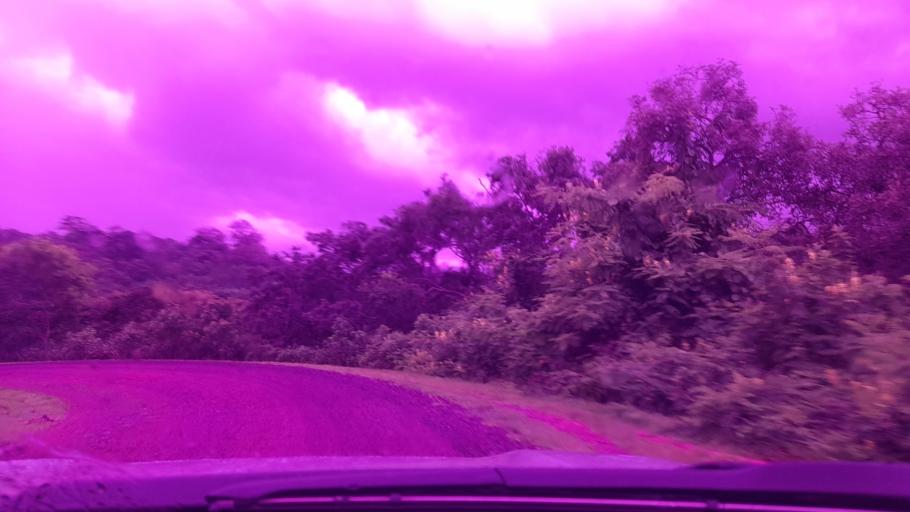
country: ET
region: Oromiya
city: Metu
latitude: 8.4365
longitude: 35.6165
